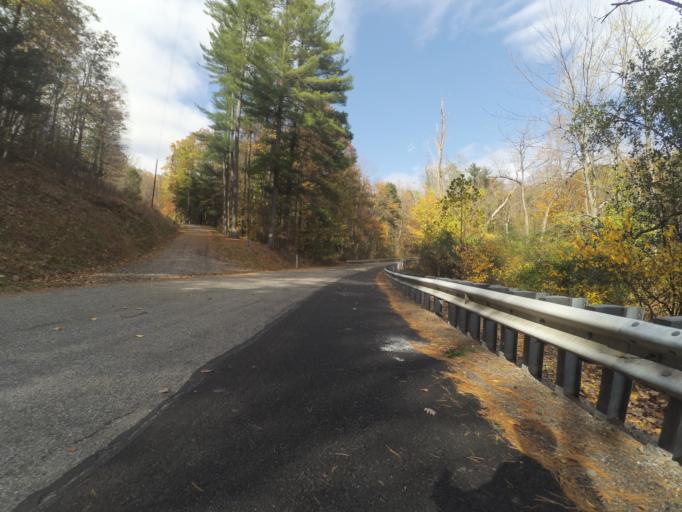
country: US
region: Pennsylvania
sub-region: Centre County
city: Stormstown
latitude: 40.8675
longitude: -77.9894
